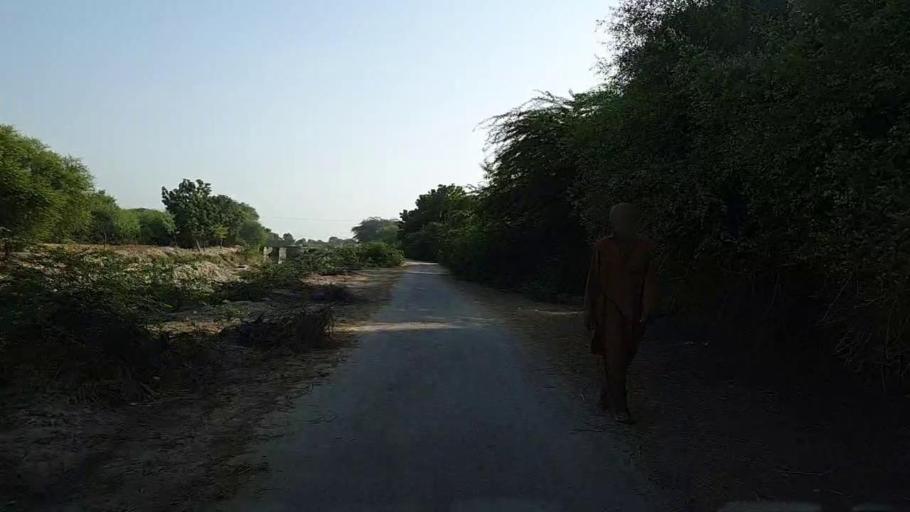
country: PK
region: Sindh
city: Kario
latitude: 24.7800
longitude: 68.6677
